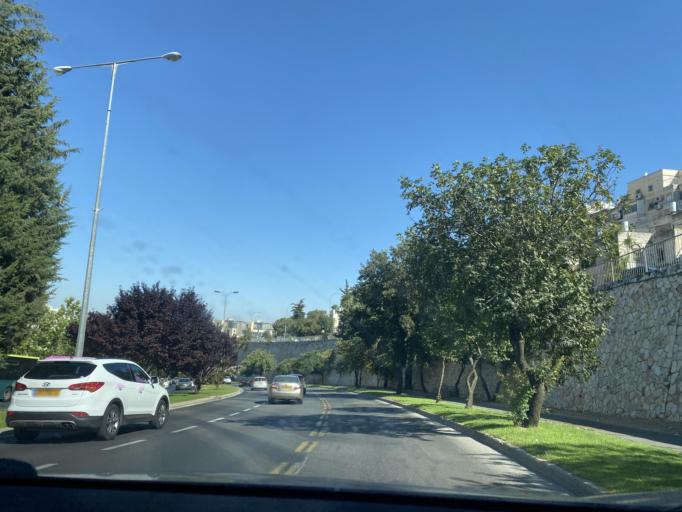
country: PS
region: West Bank
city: Bayt Iksa
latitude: 31.8206
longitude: 35.1899
